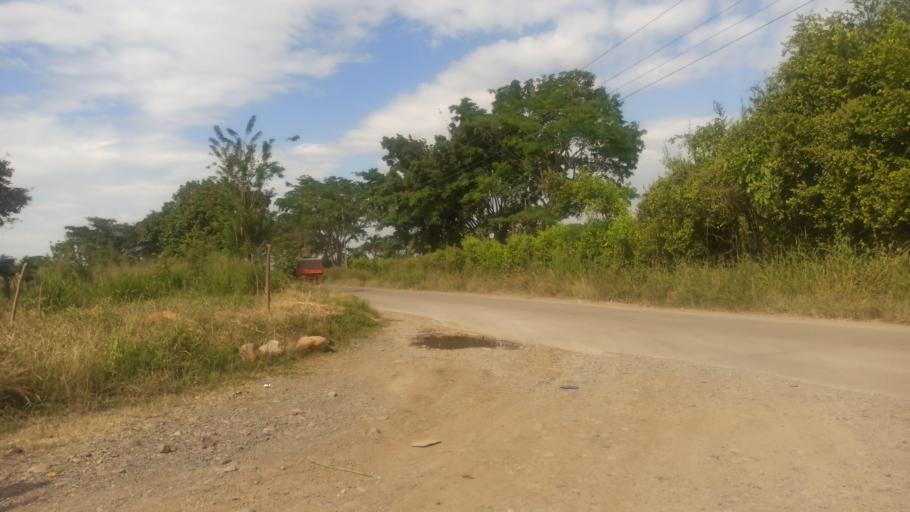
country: CO
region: Valle del Cauca
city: Jamundi
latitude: 3.1712
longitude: -76.5909
